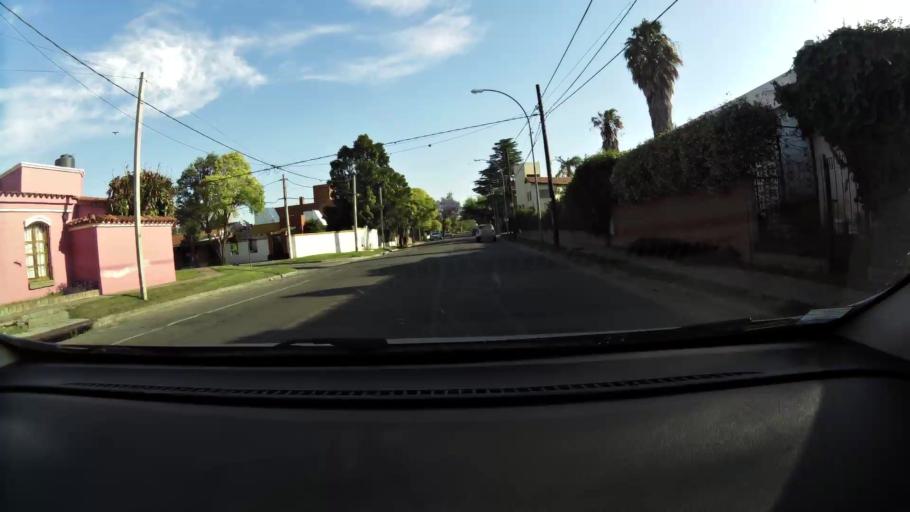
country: AR
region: Cordoba
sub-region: Departamento de Capital
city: Cordoba
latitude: -31.3662
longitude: -64.2263
